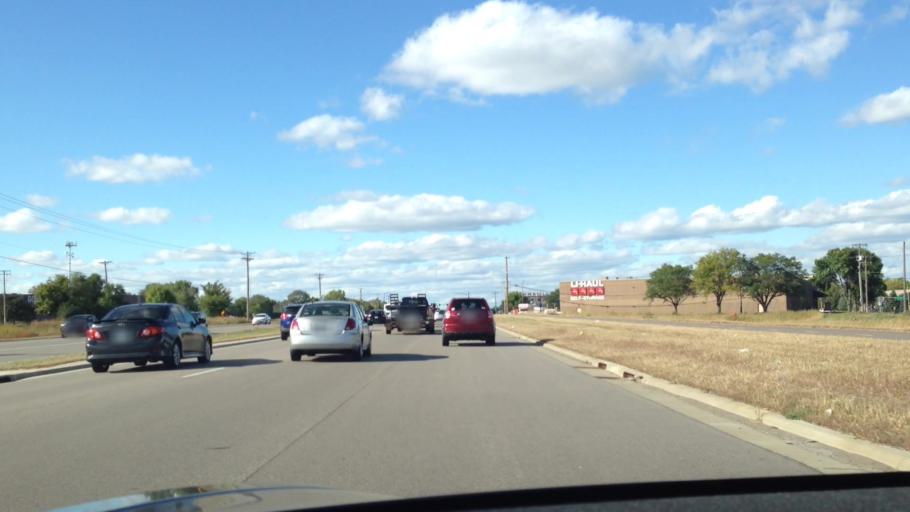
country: US
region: Minnesota
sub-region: Hennepin County
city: Brooklyn Park
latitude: 45.0801
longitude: -93.3748
